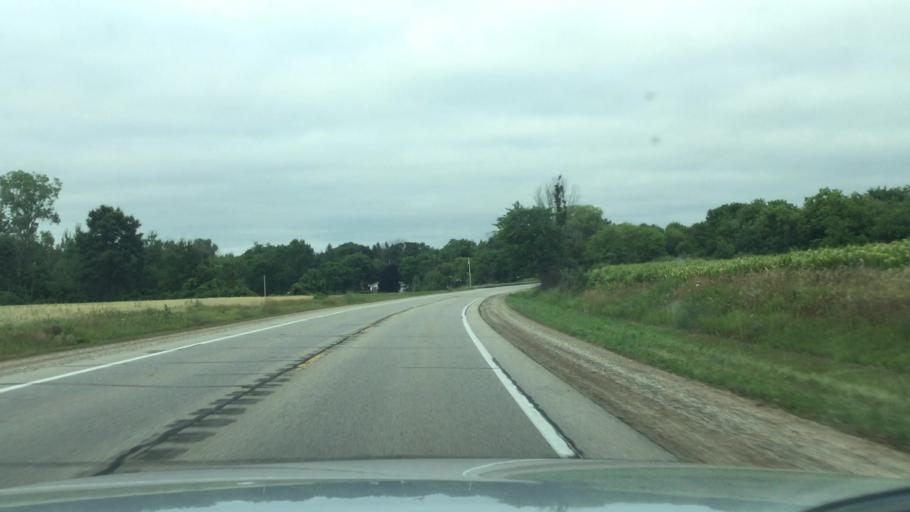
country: US
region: Michigan
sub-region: Montcalm County
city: Stanton
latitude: 43.1721
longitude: -85.1183
